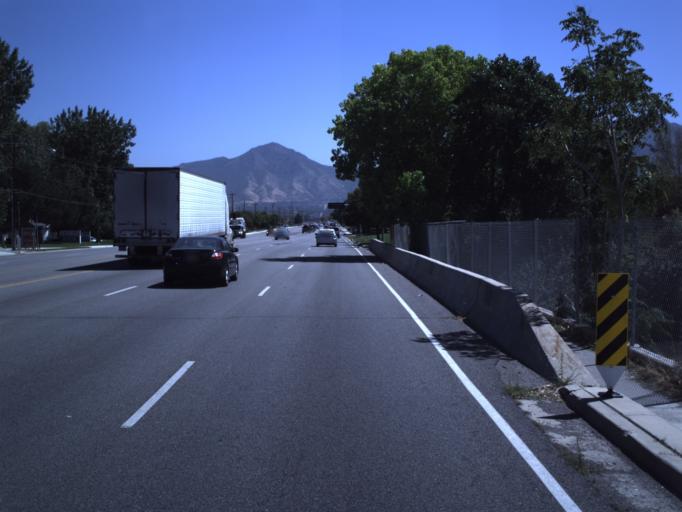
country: US
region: Utah
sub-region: Salt Lake County
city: Centerfield
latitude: 40.6993
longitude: -111.9250
